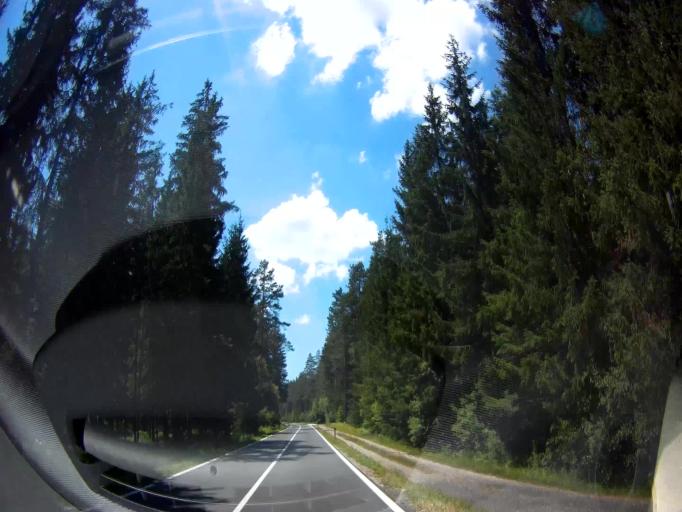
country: AT
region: Carinthia
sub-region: Politischer Bezirk Volkermarkt
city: Bleiburg/Pliberk
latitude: 46.6033
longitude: 14.7446
